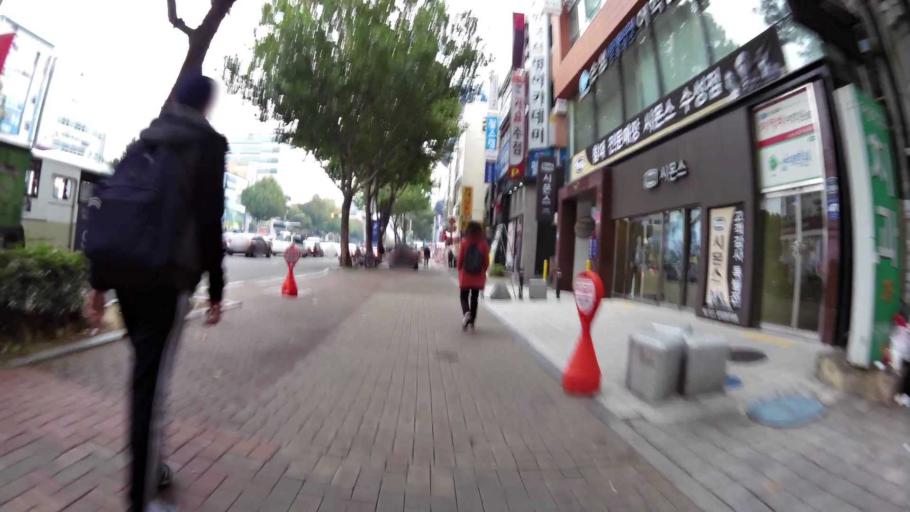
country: KR
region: Daegu
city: Daegu
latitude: 35.8587
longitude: 128.6349
